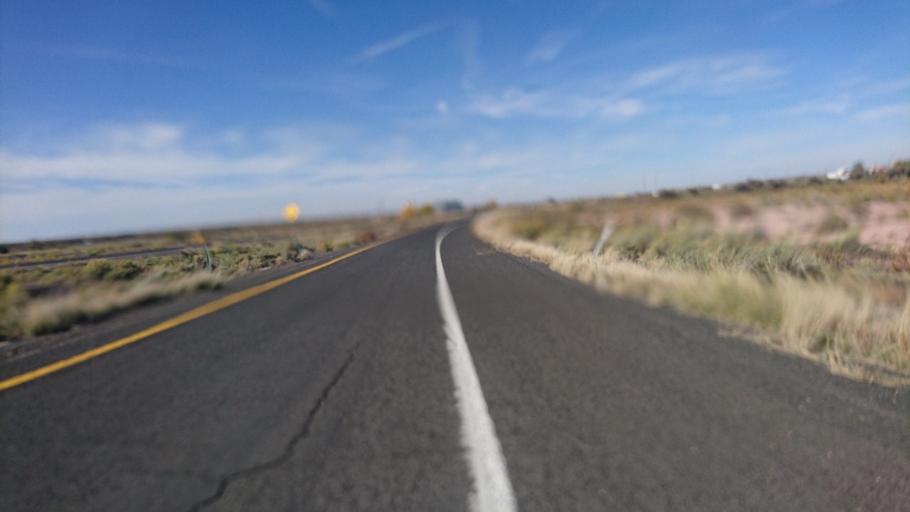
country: US
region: Arizona
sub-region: Navajo County
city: Joseph City
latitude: 34.9572
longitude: -110.3532
